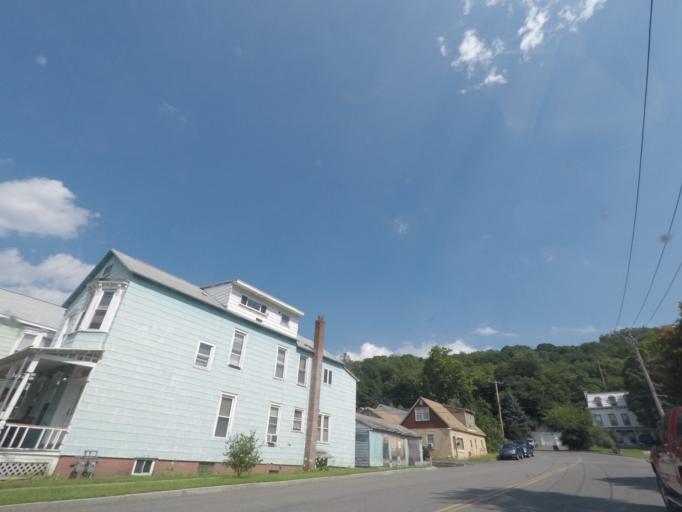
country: US
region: New York
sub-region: Saratoga County
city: Waterford
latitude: 42.7717
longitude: -73.6707
